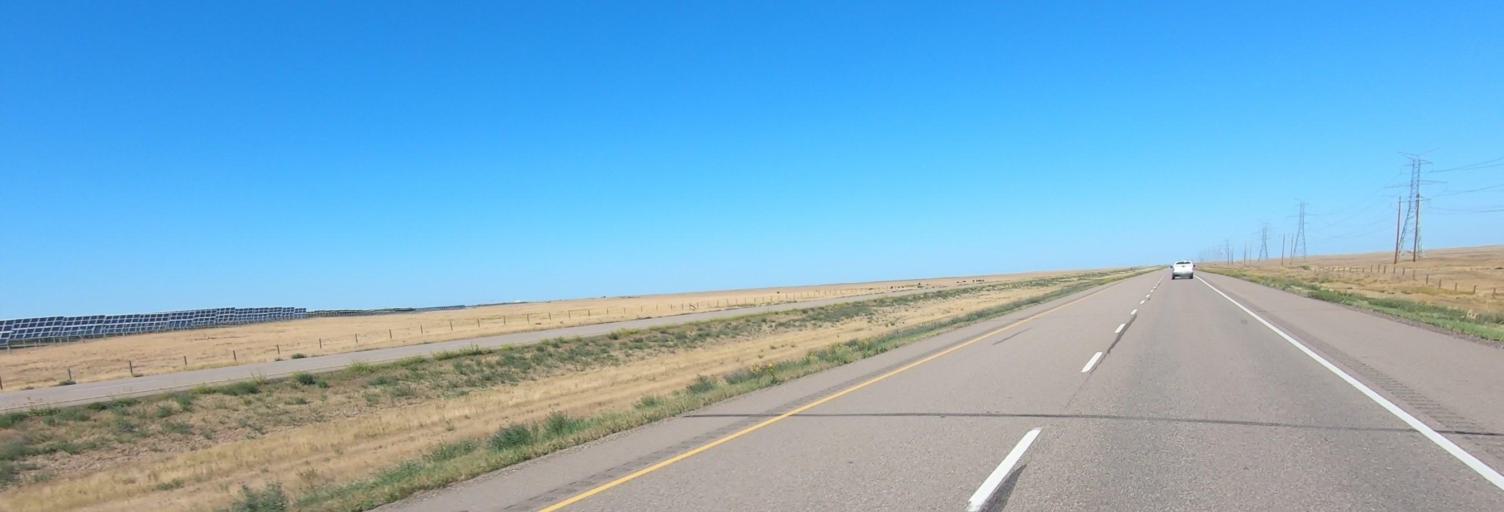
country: CA
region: Alberta
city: Bow Island
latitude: 50.2744
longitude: -111.2707
